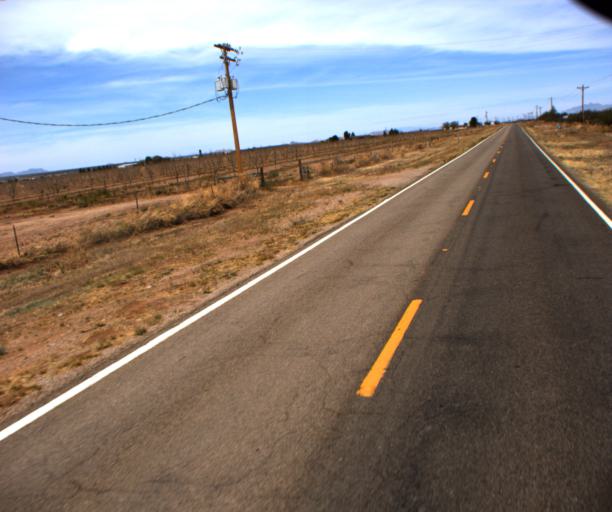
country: US
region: Arizona
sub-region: Cochise County
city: Bisbee
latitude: 31.7213
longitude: -109.6871
